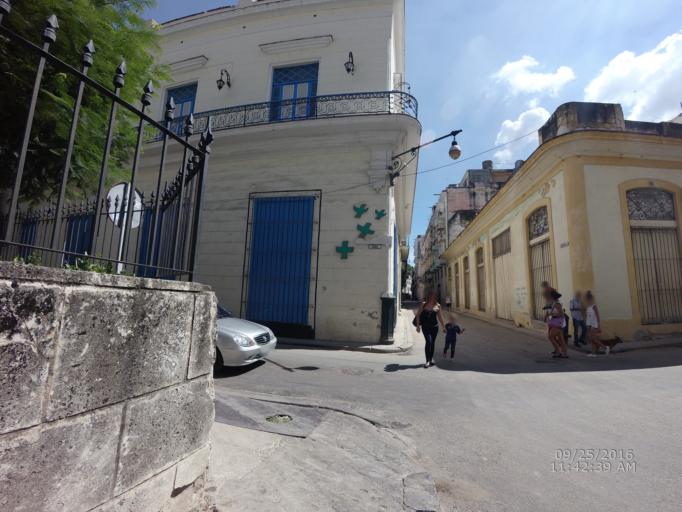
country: CU
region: La Habana
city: La Habana Vieja
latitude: 23.1376
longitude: -82.3519
